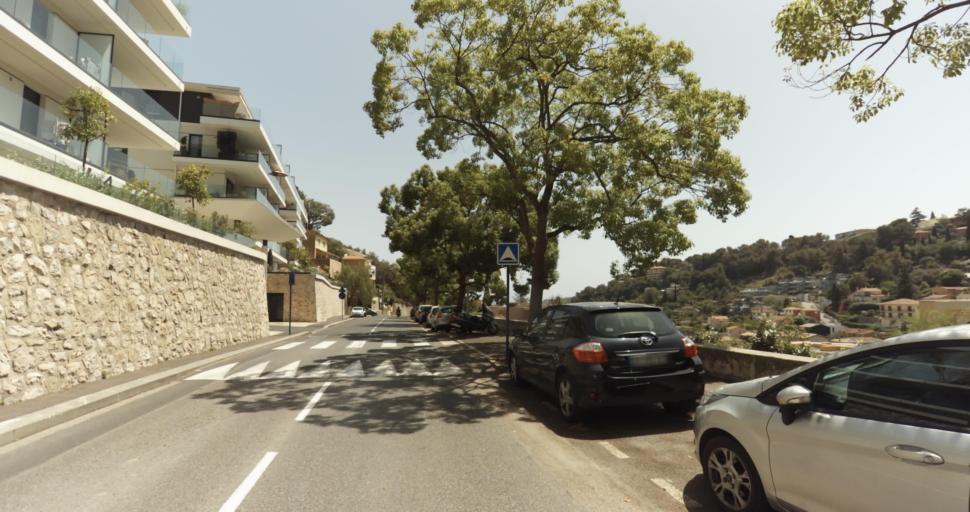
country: FR
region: Provence-Alpes-Cote d'Azur
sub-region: Departement des Alpes-Maritimes
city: Roquebrune-Cap-Martin
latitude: 43.7716
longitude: 7.4786
